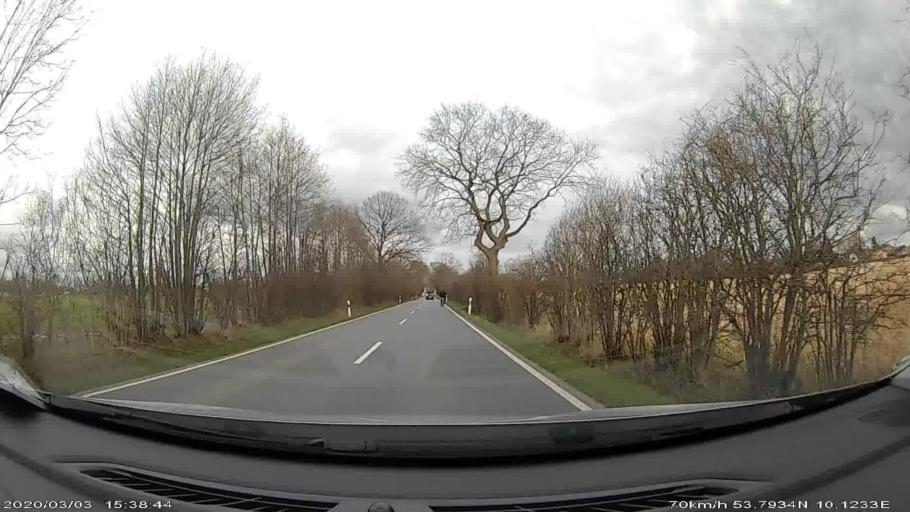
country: DE
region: Schleswig-Holstein
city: Nahe
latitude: 53.7929
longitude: 10.1217
